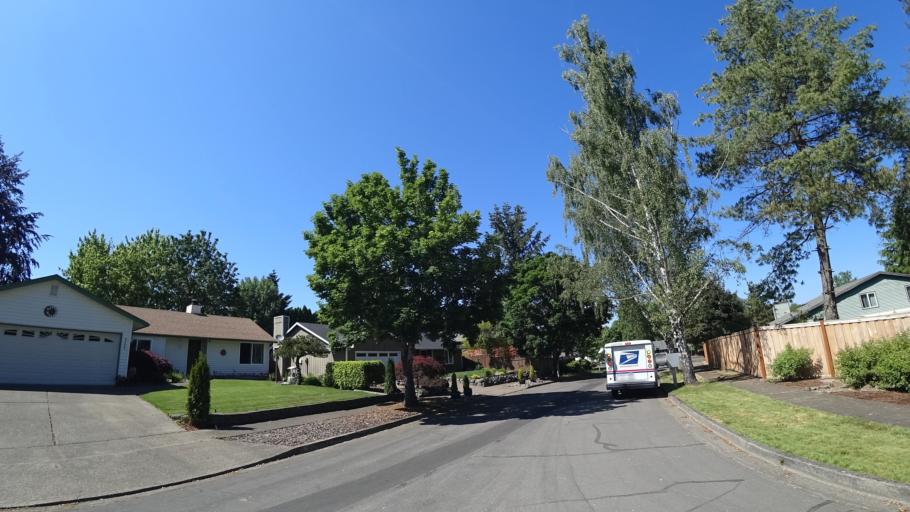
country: US
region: Oregon
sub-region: Washington County
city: Tigard
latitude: 45.4525
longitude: -122.7981
